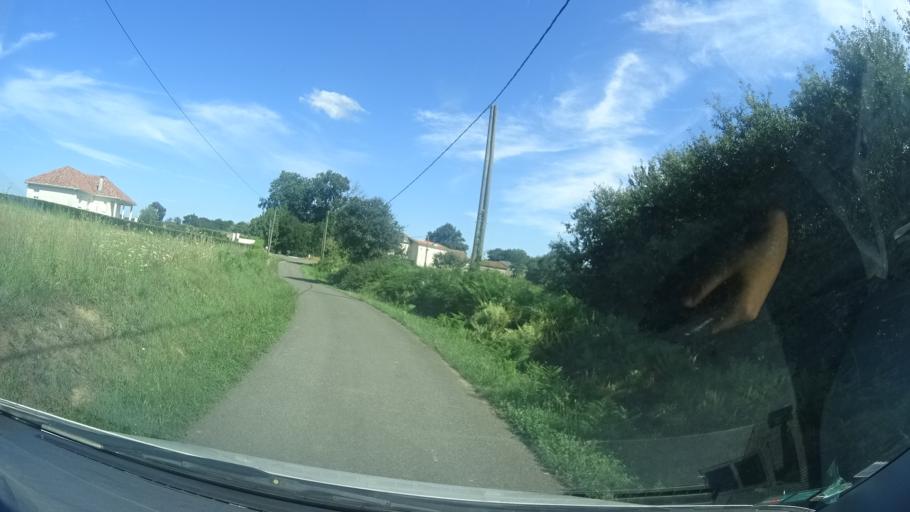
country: FR
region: Aquitaine
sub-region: Departement des Pyrenees-Atlantiques
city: Mont
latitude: 43.5021
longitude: -0.6771
